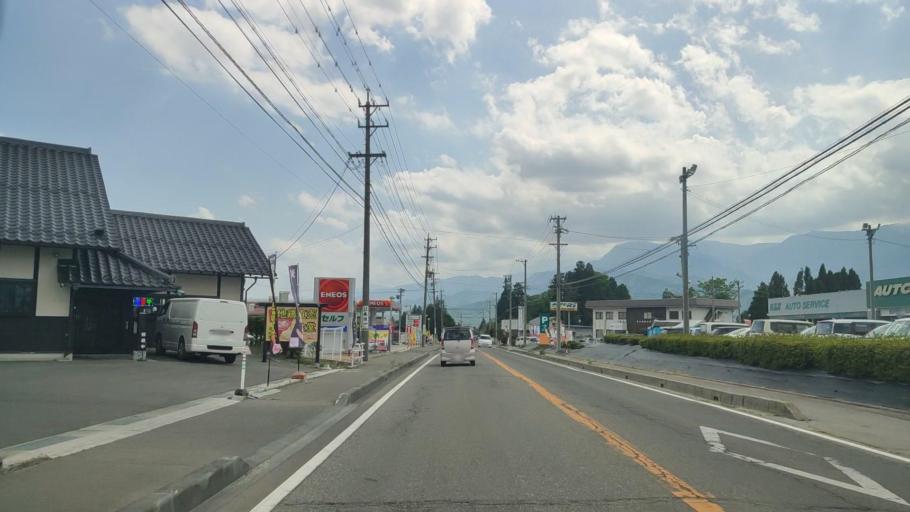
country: JP
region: Nagano
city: Omachi
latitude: 36.4776
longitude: 137.8494
